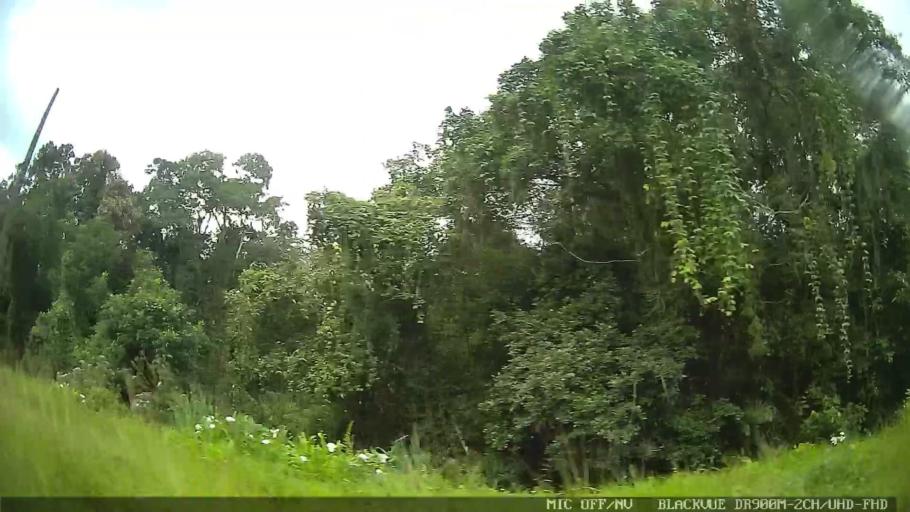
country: BR
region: Sao Paulo
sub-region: Itanhaem
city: Itanhaem
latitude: -24.1443
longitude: -46.7766
